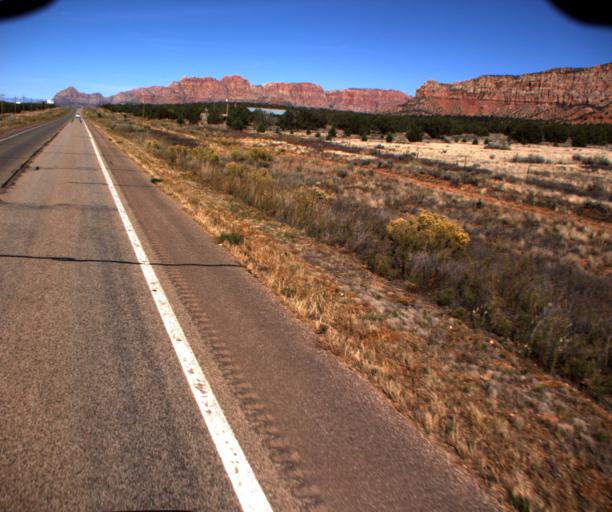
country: US
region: Arizona
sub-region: Mohave County
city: Colorado City
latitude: 36.9505
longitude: -112.9589
